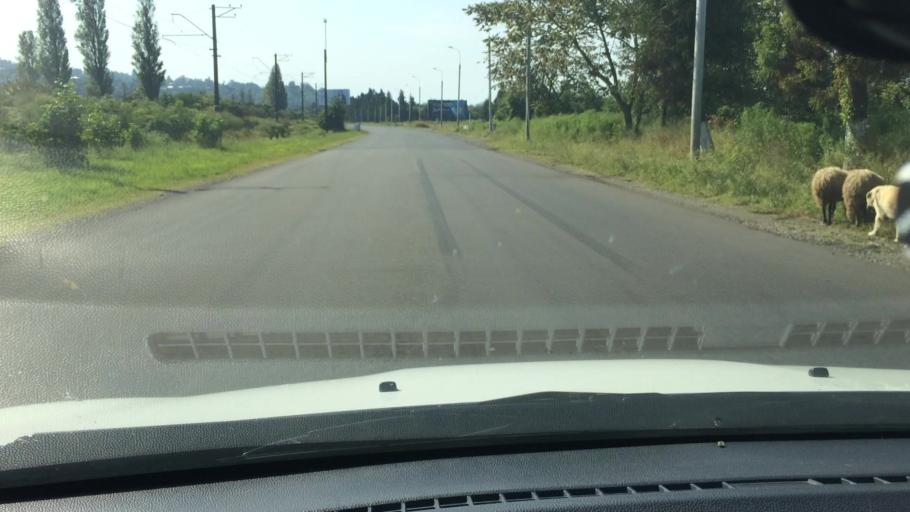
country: GE
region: Ajaria
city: Kobuleti
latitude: 41.7925
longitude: 41.7694
